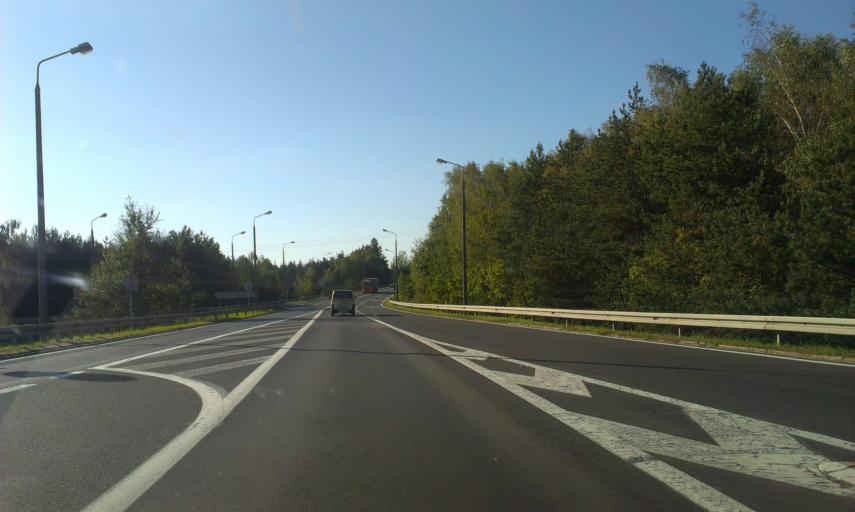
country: PL
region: Kujawsko-Pomorskie
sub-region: Powiat swiecki
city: Swiecie
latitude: 53.4085
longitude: 18.3809
